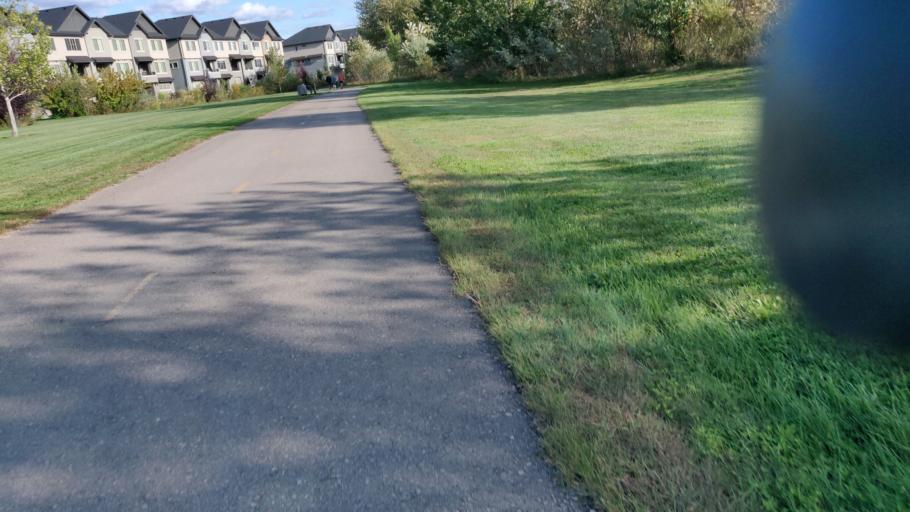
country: US
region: Idaho
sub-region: Ada County
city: Boise
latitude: 43.5748
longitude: -116.1466
